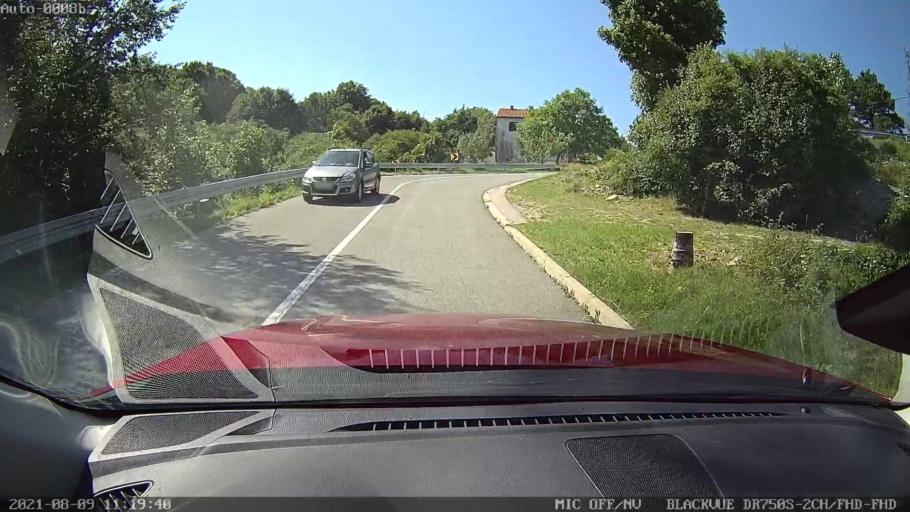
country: HR
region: Istarska
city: Lovran
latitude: 45.3054
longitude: 14.1938
